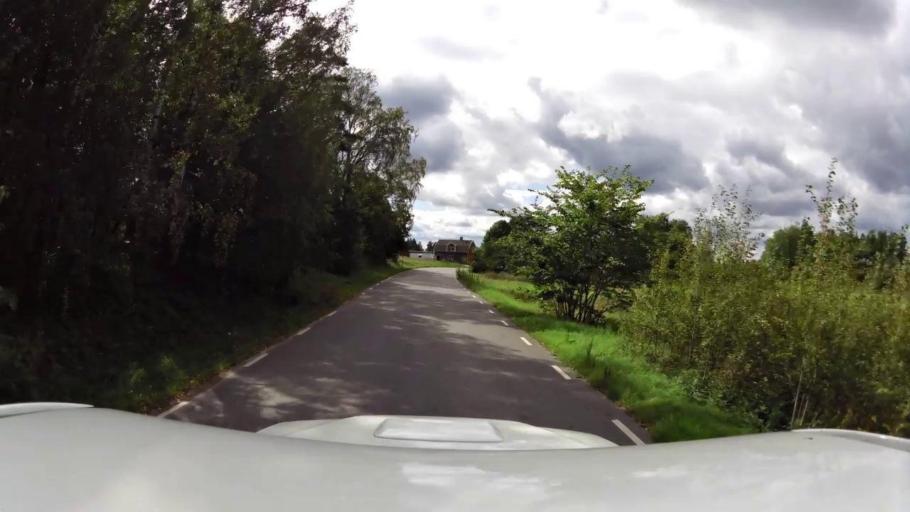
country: SE
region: OEstergoetland
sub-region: Linkopings Kommun
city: Malmslatt
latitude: 58.3669
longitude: 15.5603
